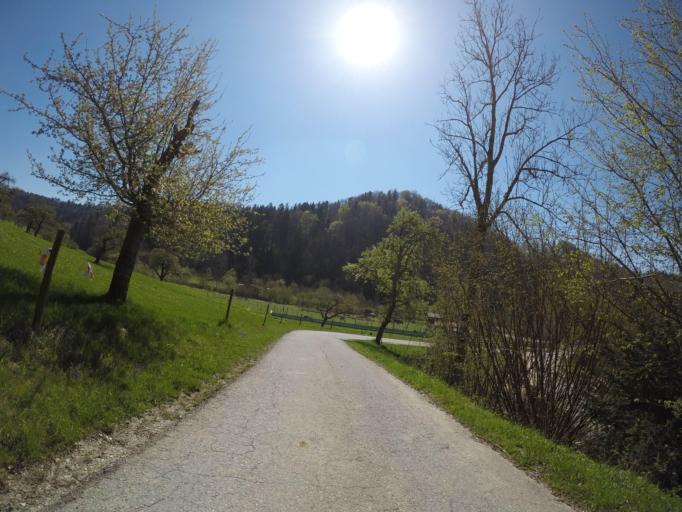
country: DE
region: Baden-Wuerttemberg
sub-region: Tuebingen Region
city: Horgenzell
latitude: 47.7870
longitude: 9.4426
